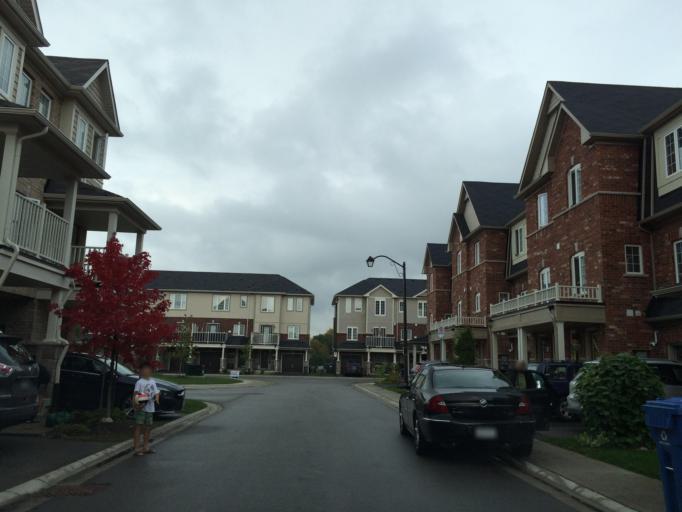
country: CA
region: Ontario
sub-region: Wellington County
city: Guelph
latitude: 43.5254
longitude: -80.1916
